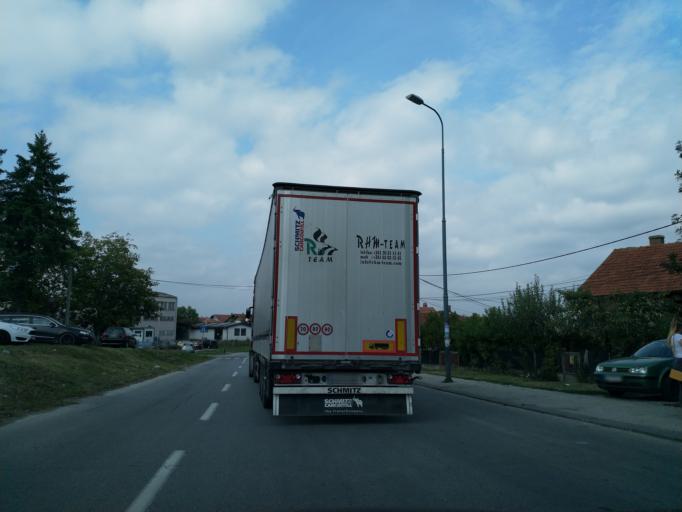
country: RS
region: Central Serbia
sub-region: Sumadijski Okrug
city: Kragujevac
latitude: 44.0297
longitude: 20.9166
